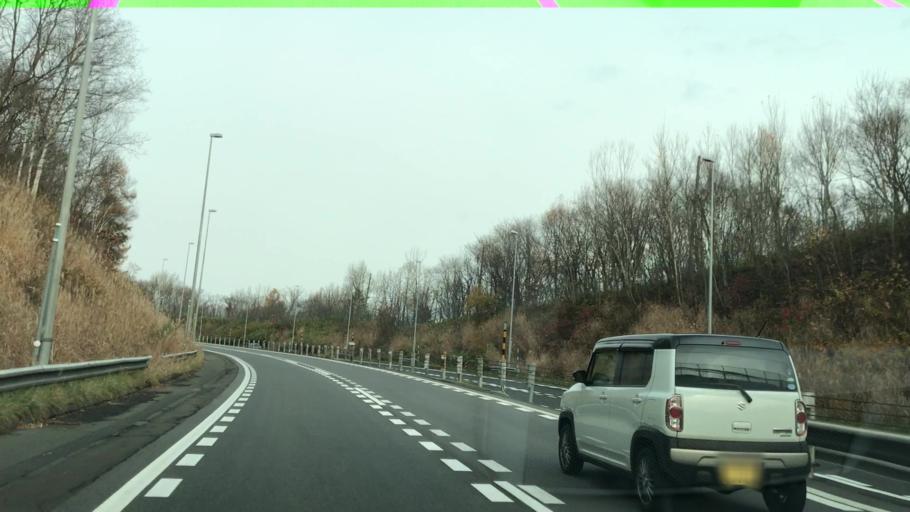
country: JP
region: Hokkaido
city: Otaru
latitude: 43.1599
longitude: 141.1084
